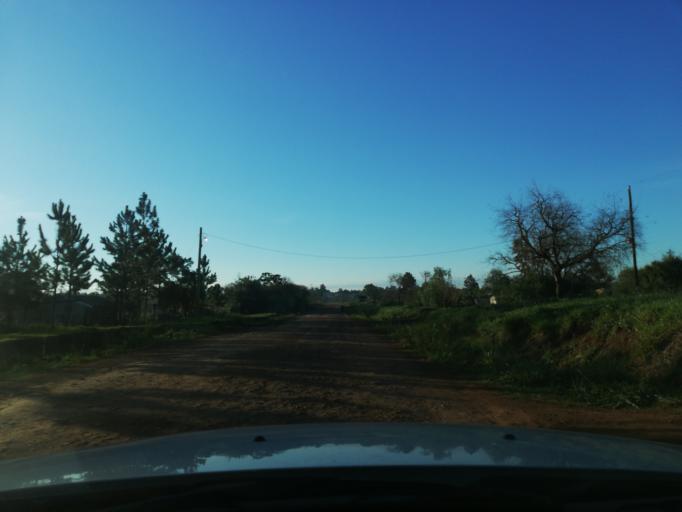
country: AR
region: Misiones
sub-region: Departamento de Capital
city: Posadas
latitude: -27.4757
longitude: -55.9709
